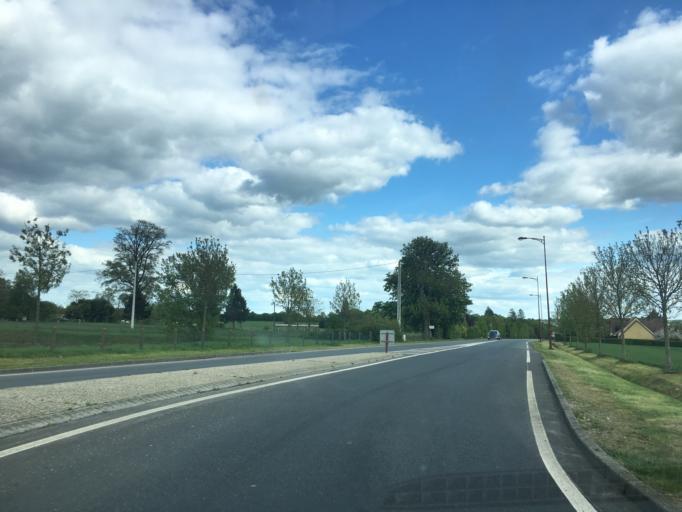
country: FR
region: Lower Normandy
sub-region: Departement de l'Orne
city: Rai
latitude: 48.7743
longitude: 0.6100
